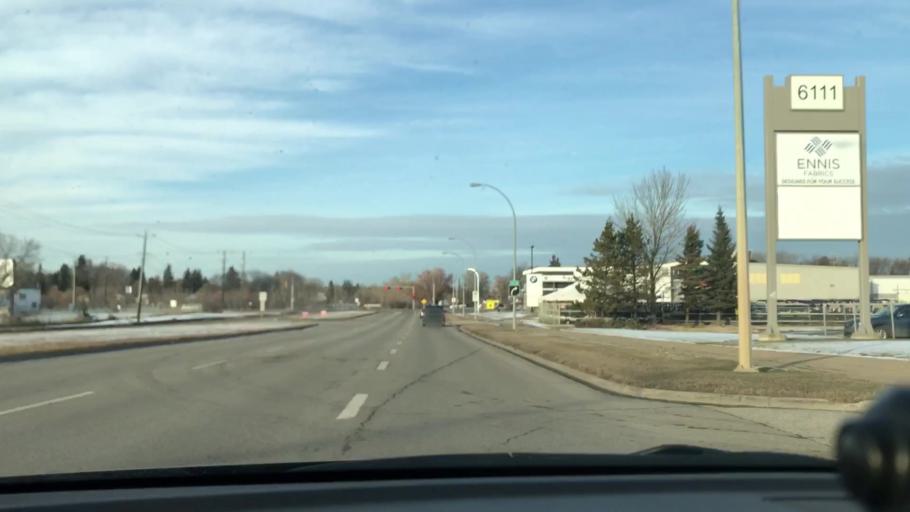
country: CA
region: Alberta
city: Edmonton
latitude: 53.4979
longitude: -113.4670
